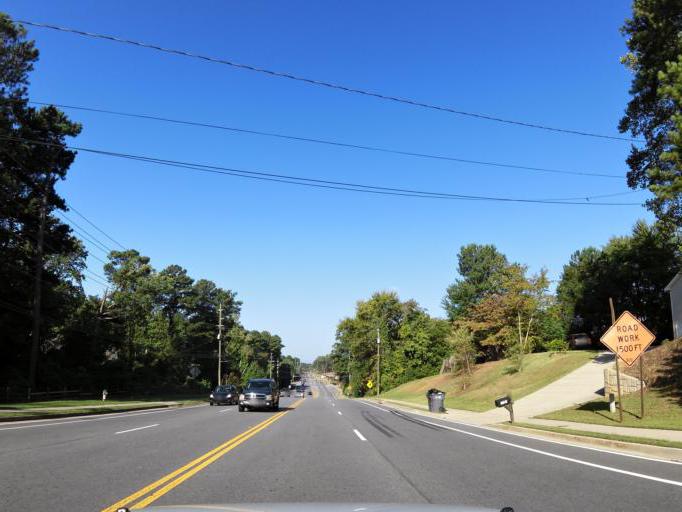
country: US
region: Georgia
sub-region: Cobb County
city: Kennesaw
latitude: 33.9982
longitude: -84.6450
